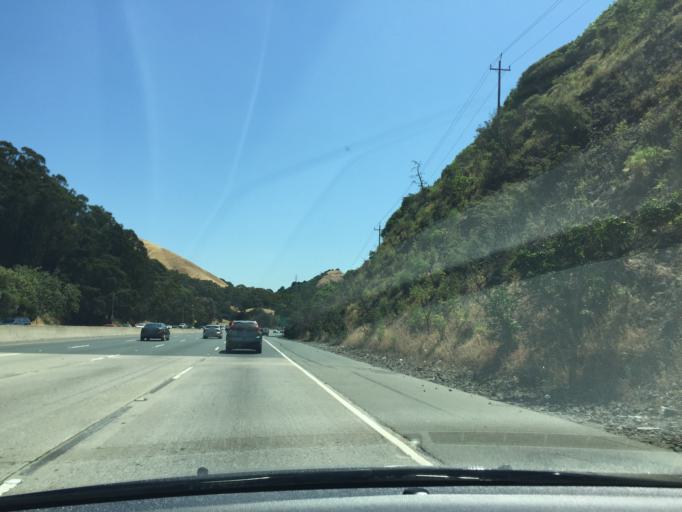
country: US
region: California
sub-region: Contra Costa County
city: Orinda
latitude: 37.8664
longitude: -122.2052
